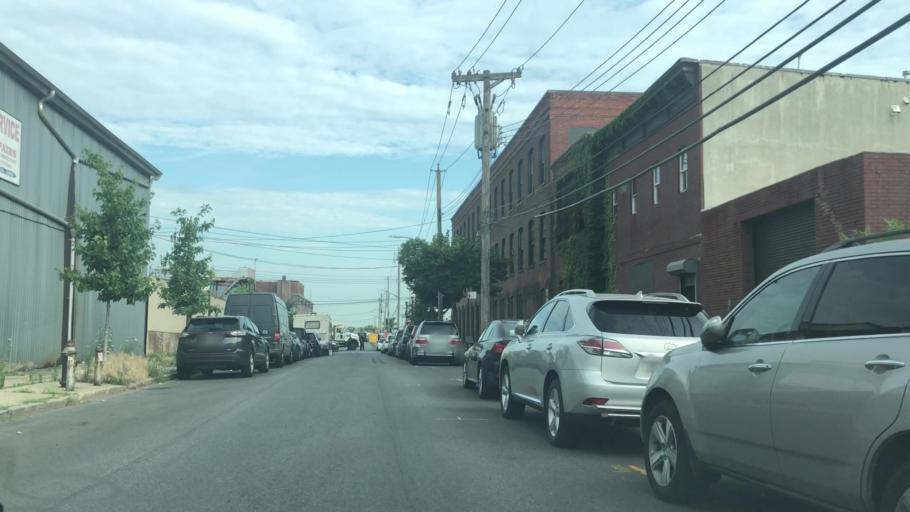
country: US
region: New York
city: New York City
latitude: 40.6786
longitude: -74.0148
